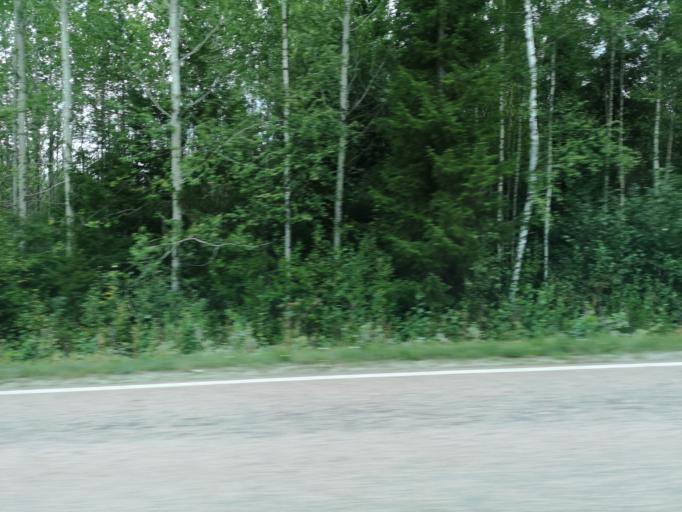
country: FI
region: Central Finland
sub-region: Jyvaeskylae
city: Hankasalmi
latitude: 62.3589
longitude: 26.5540
